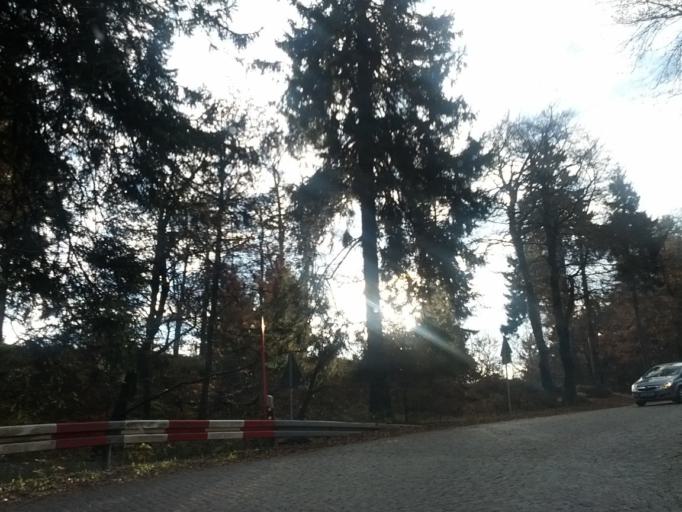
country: DE
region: Thuringia
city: Brotterode
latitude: 50.8494
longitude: 10.4712
